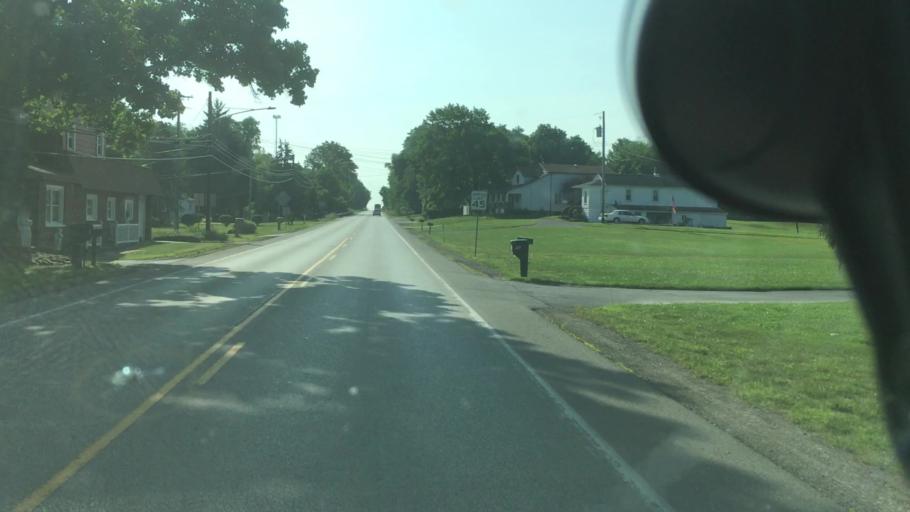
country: US
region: Pennsylvania
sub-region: Lawrence County
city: Bessemer
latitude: 41.0123
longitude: -80.4834
